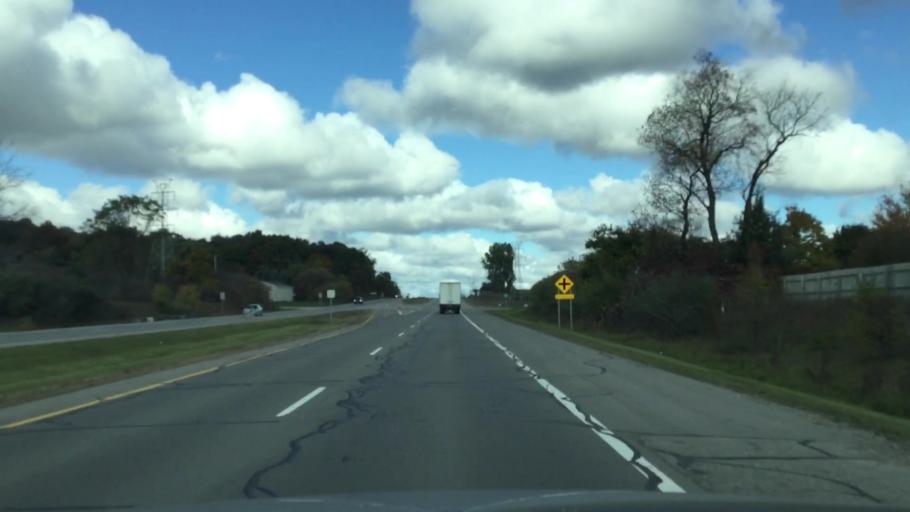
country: US
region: Michigan
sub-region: Oakland County
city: Oxford
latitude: 42.8819
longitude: -83.3042
